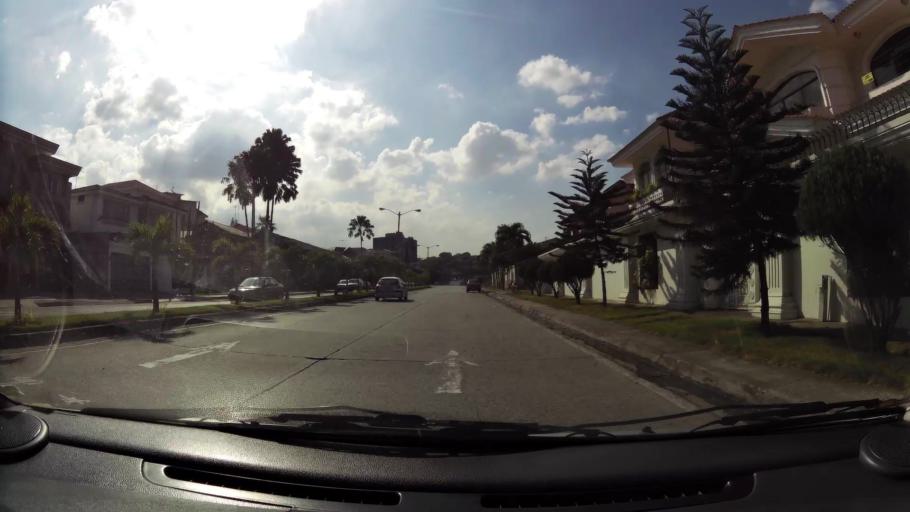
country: EC
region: Guayas
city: Santa Lucia
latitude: -2.1623
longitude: -79.9464
